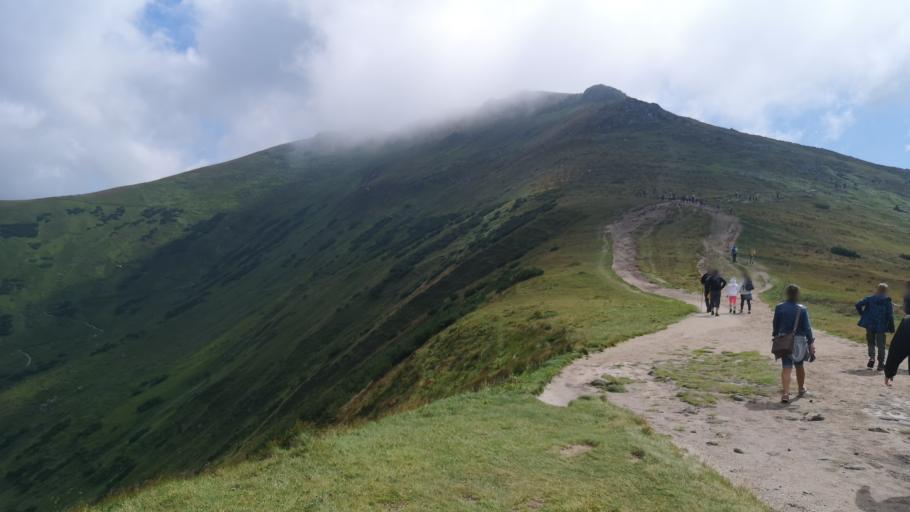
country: SK
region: Banskobystricky
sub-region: Okres Banska Bystrica
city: Brezno
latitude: 48.9401
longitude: 19.6192
